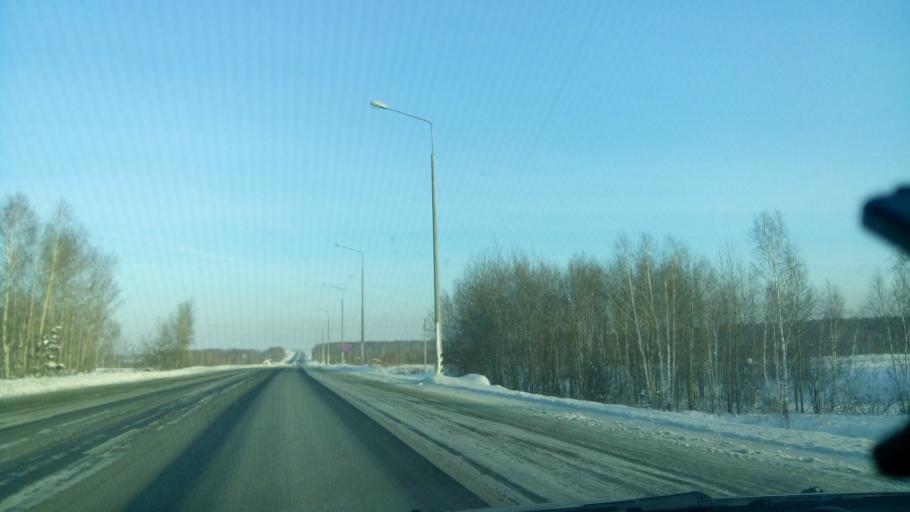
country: RU
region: Chelyabinsk
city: Dolgoderevenskoye
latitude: 55.3679
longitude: 61.3172
